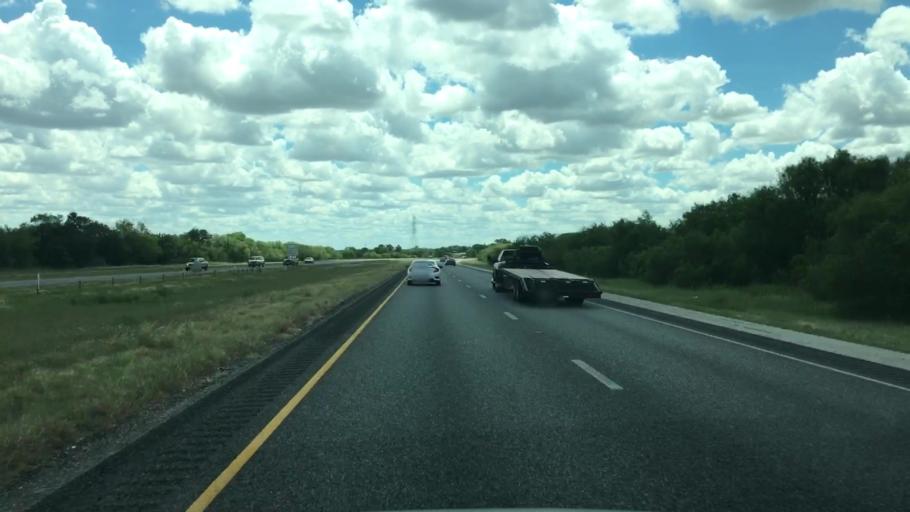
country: US
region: Texas
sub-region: Bexar County
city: Elmendorf
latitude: 29.2559
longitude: -98.3952
